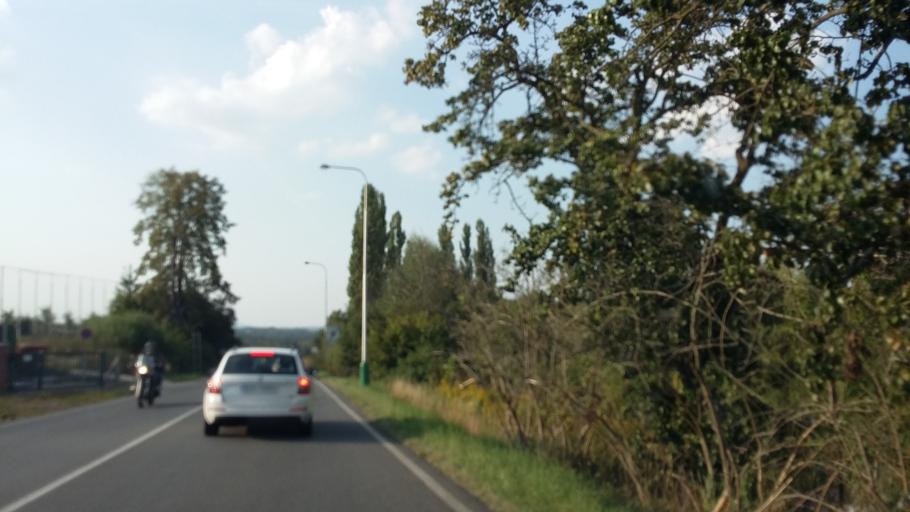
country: CZ
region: Central Bohemia
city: Kosmonosy
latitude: 50.4481
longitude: 14.9309
